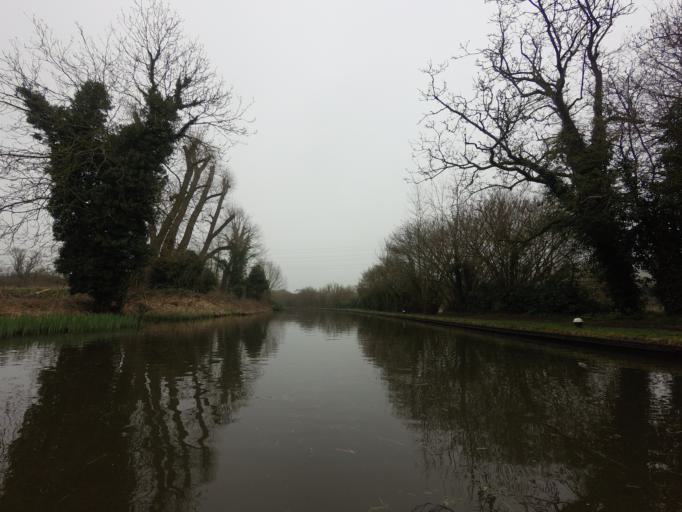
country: GB
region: England
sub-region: Hertfordshire
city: Berkhamsted
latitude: 51.7522
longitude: -0.5393
